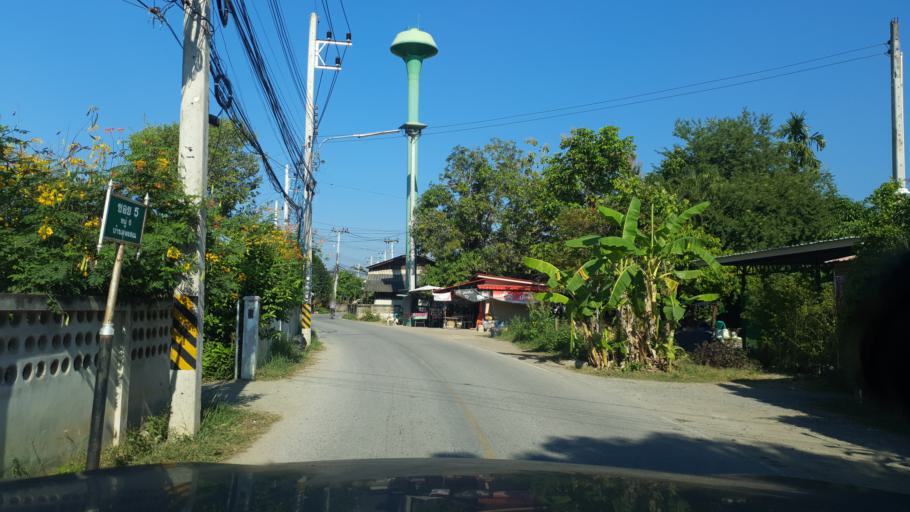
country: TH
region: Chiang Mai
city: Saraphi
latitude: 18.7297
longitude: 99.0620
